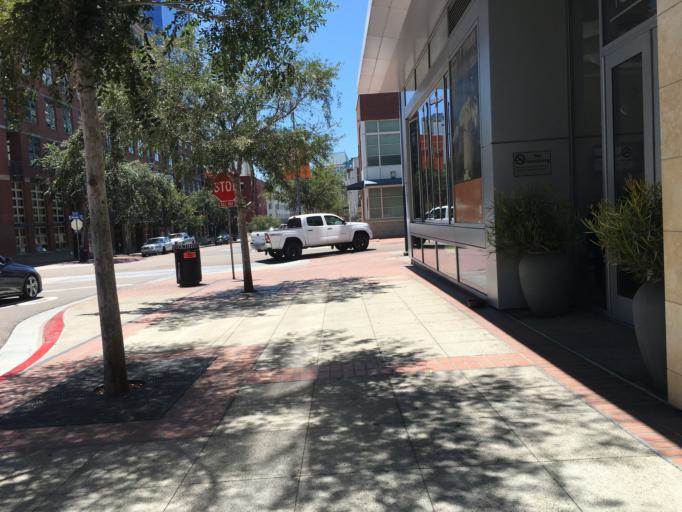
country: US
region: California
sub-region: San Diego County
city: San Diego
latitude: 32.7106
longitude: -117.1562
